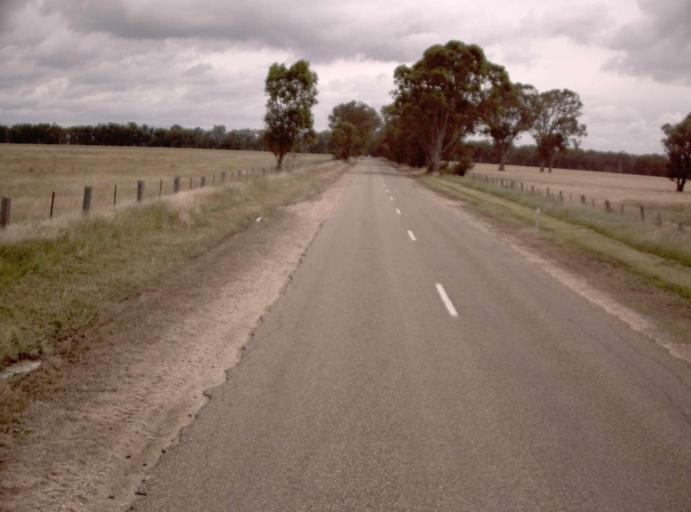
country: AU
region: Victoria
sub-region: Wellington
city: Sale
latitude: -37.8775
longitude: 147.0659
